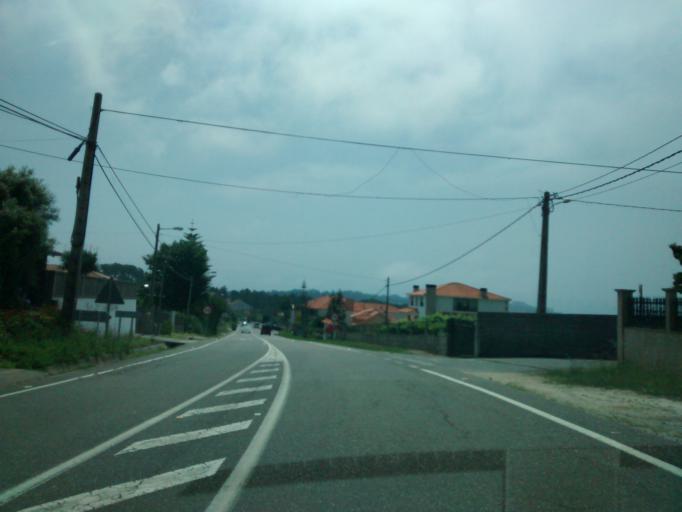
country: ES
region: Galicia
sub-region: Provincia de Pontevedra
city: Sanxenxo
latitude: 42.4044
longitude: -8.8524
